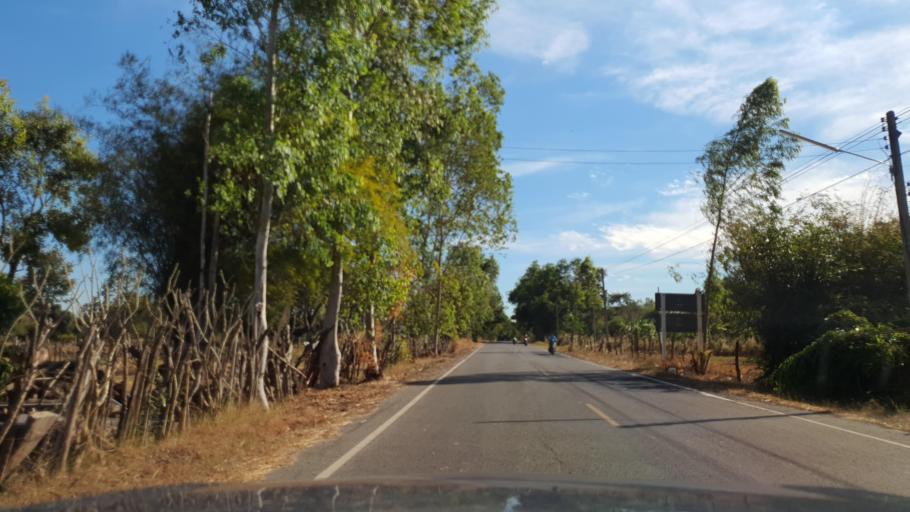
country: TH
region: Kalasin
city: Khao Wong
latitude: 16.6194
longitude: 104.1356
